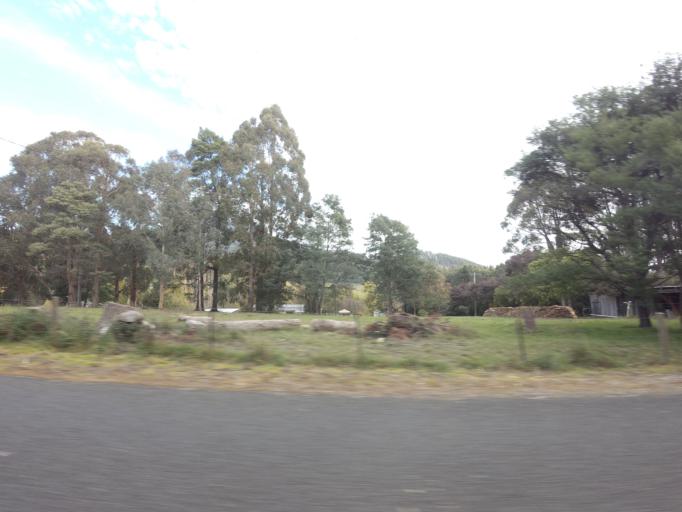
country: AU
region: Tasmania
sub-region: Meander Valley
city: Deloraine
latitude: -41.6206
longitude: 146.6999
